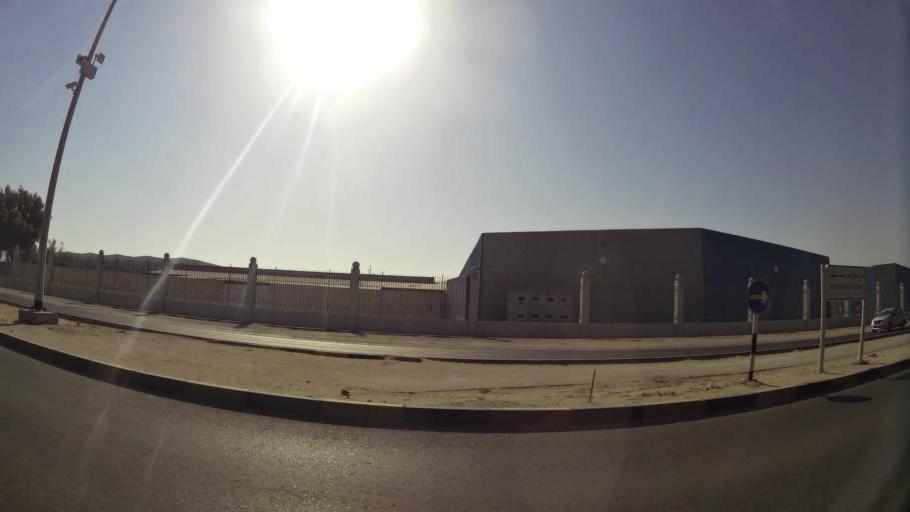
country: AE
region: Ajman
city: Ajman
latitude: 25.4152
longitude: 55.4527
